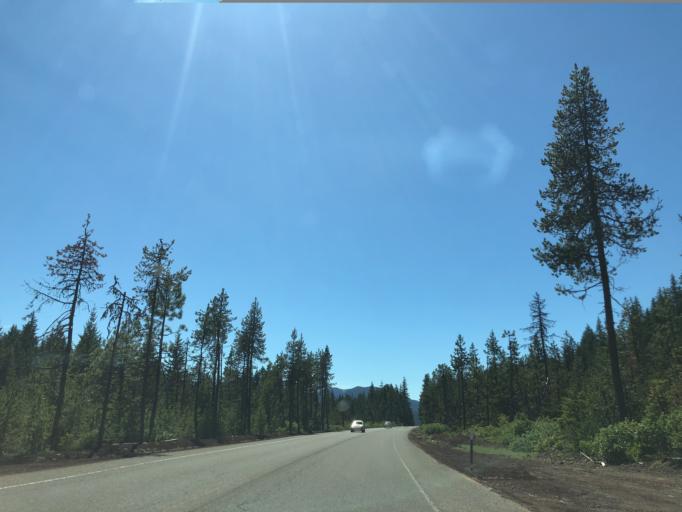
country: US
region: Oregon
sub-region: Deschutes County
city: Sisters
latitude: 44.4331
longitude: -121.9561
